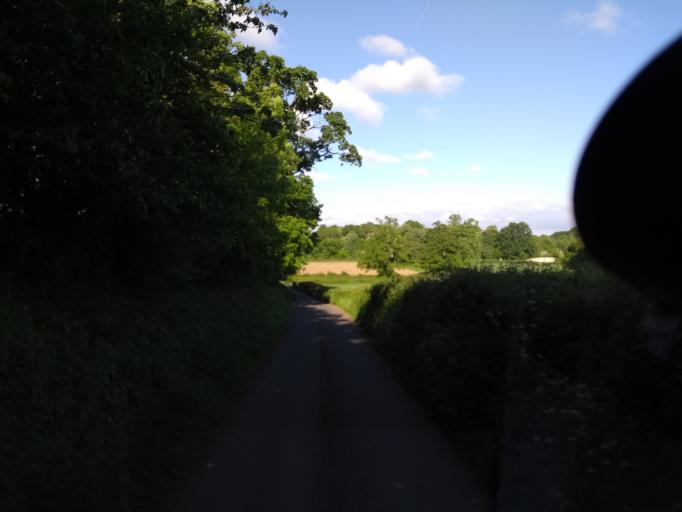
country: GB
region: England
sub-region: Somerset
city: Taunton
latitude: 50.9761
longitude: -3.1001
